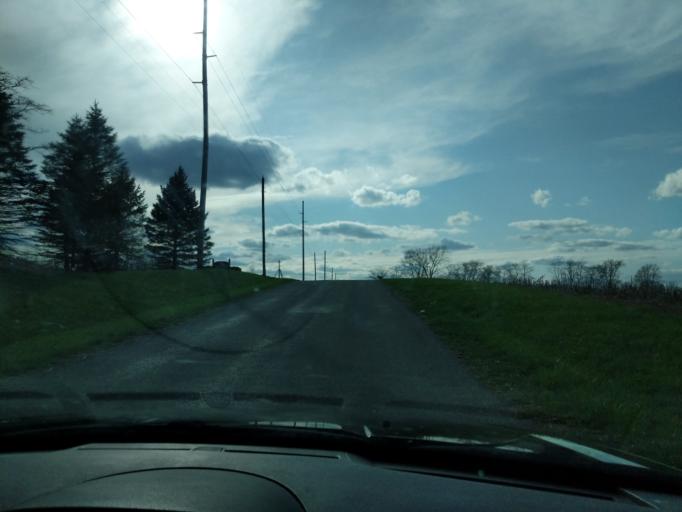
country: US
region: Ohio
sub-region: Champaign County
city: North Lewisburg
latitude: 40.1636
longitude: -83.6527
